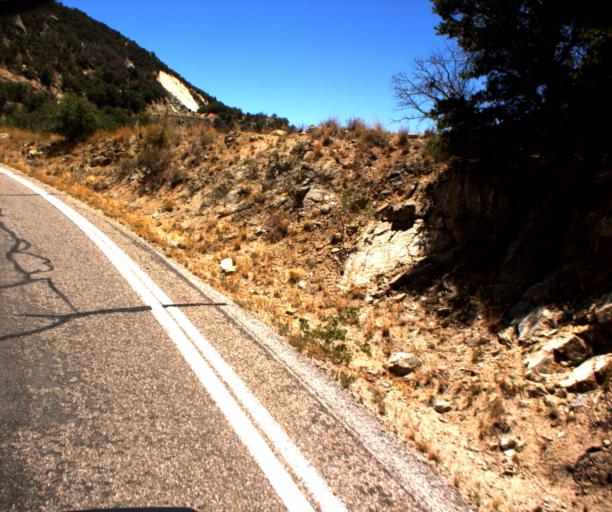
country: US
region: Arizona
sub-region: Pima County
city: Sells
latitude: 31.9615
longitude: -111.6253
